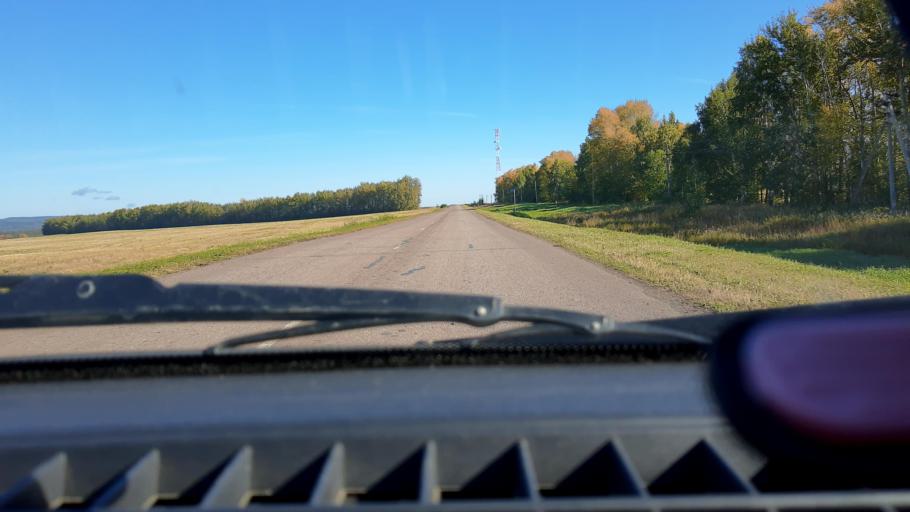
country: RU
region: Bashkortostan
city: Kushnarenkovo
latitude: 55.0688
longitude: 55.4526
